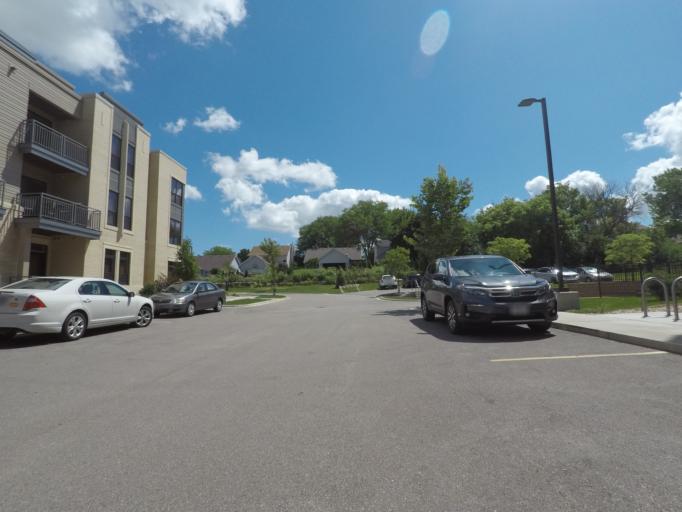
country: US
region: Wisconsin
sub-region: Dane County
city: Middleton
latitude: 43.0718
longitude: -89.5268
